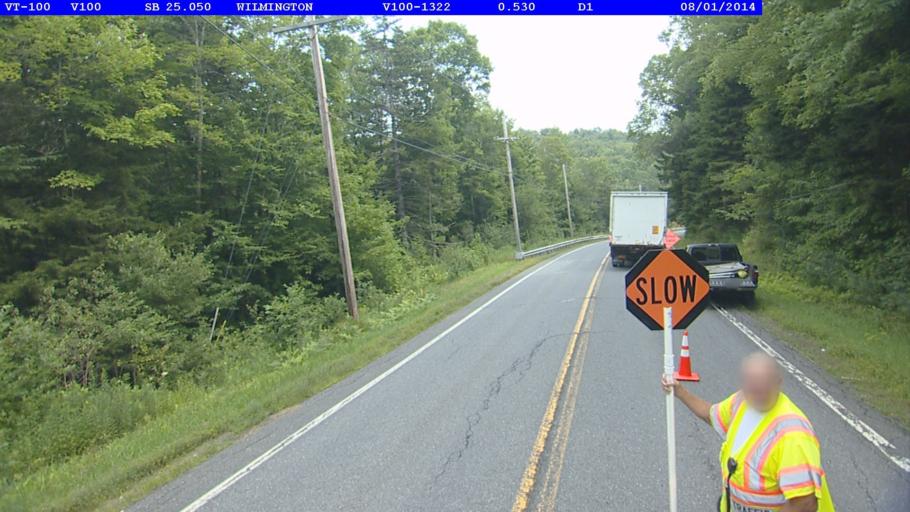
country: US
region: Vermont
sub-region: Windham County
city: Dover
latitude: 42.8351
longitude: -72.8550
